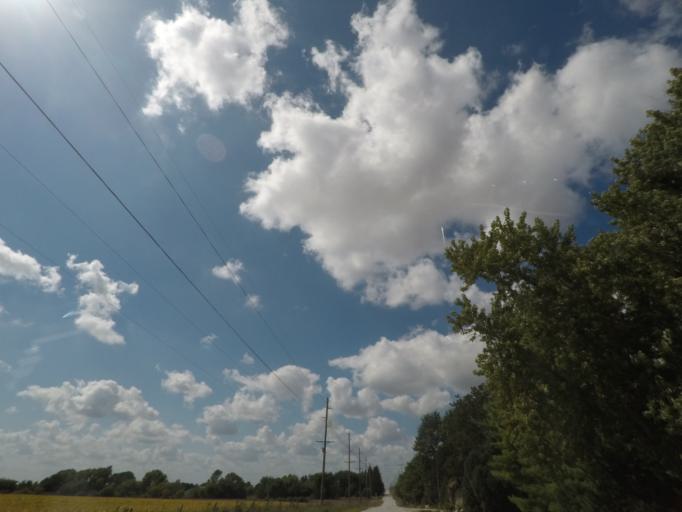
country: US
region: Iowa
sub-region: Story County
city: Nevada
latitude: 42.0344
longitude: -93.3915
